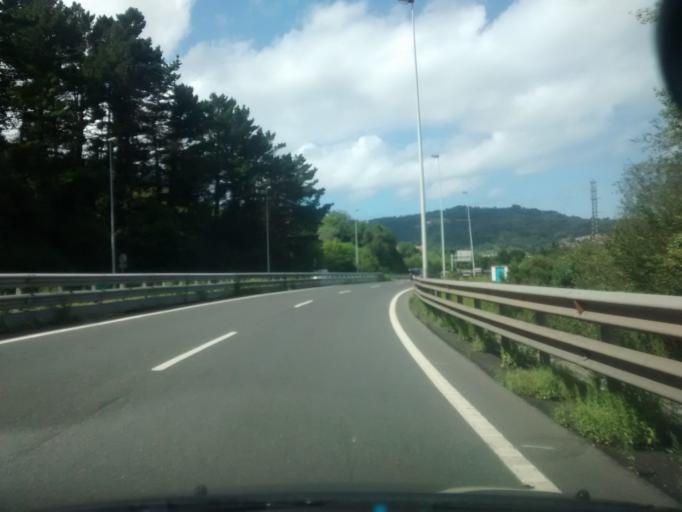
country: ES
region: Basque Country
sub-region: Provincia de Guipuzcoa
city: San Sebastian
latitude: 43.2961
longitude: -1.9992
